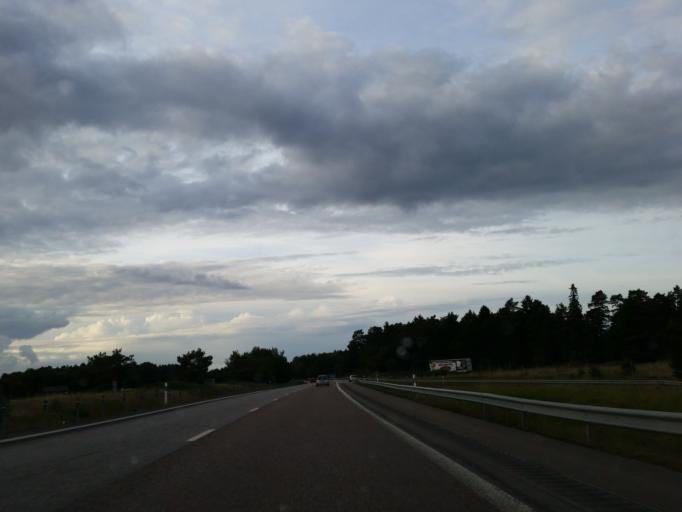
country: SE
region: Uppsala
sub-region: Knivsta Kommun
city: Knivsta
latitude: 59.7420
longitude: 17.8187
